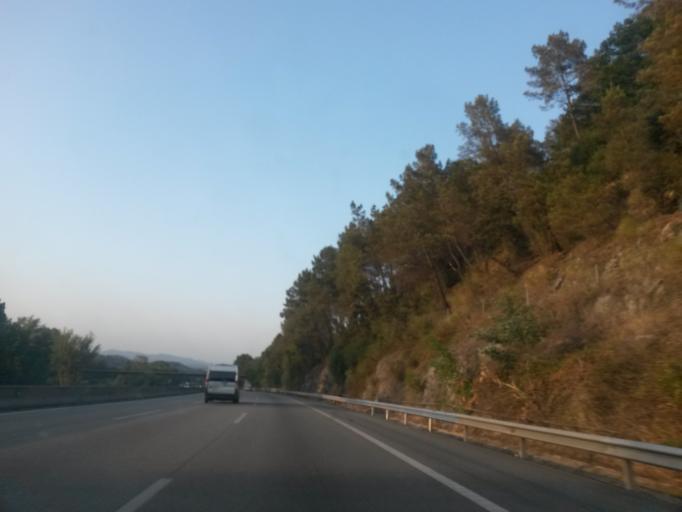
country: ES
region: Catalonia
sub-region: Provincia de Barcelona
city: Sant Celoni
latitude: 41.6940
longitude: 2.5117
